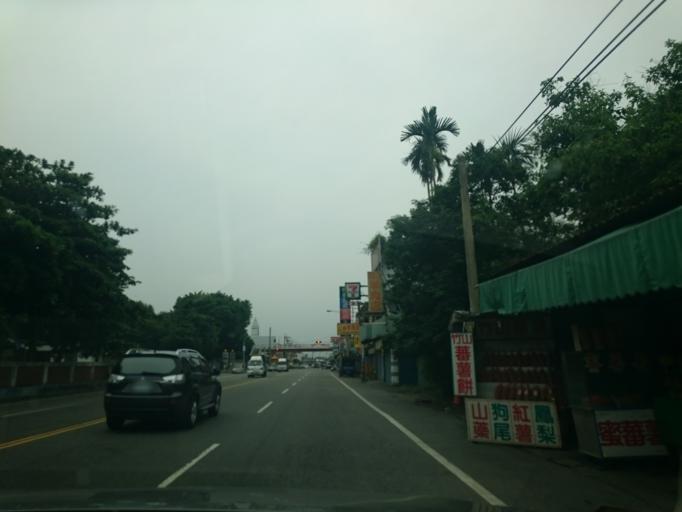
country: TW
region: Taiwan
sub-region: Nantou
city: Nantou
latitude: 23.8443
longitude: 120.6988
